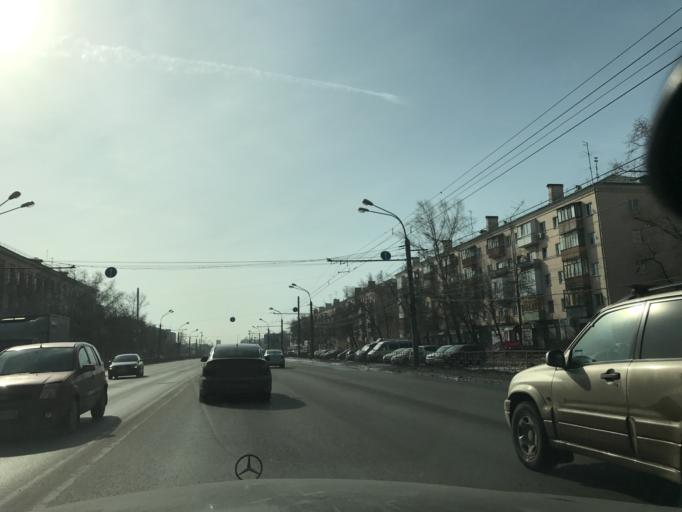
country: RU
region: Nizjnij Novgorod
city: Nizhniy Novgorod
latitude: 56.2930
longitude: 43.9338
